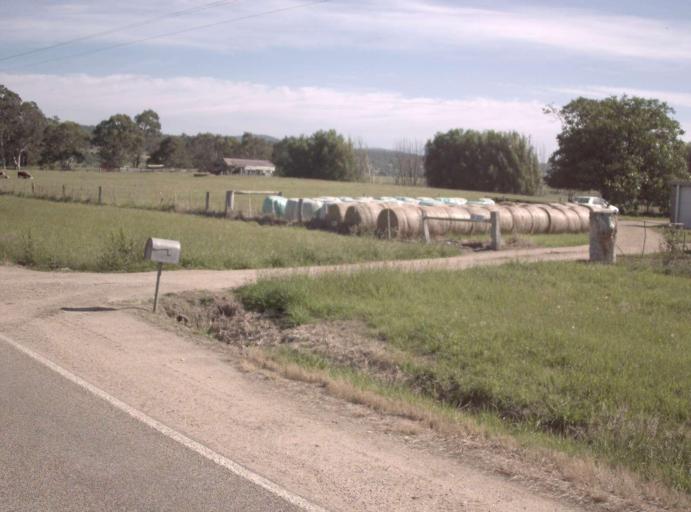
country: AU
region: Victoria
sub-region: East Gippsland
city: Bairnsdale
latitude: -37.7289
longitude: 147.8093
